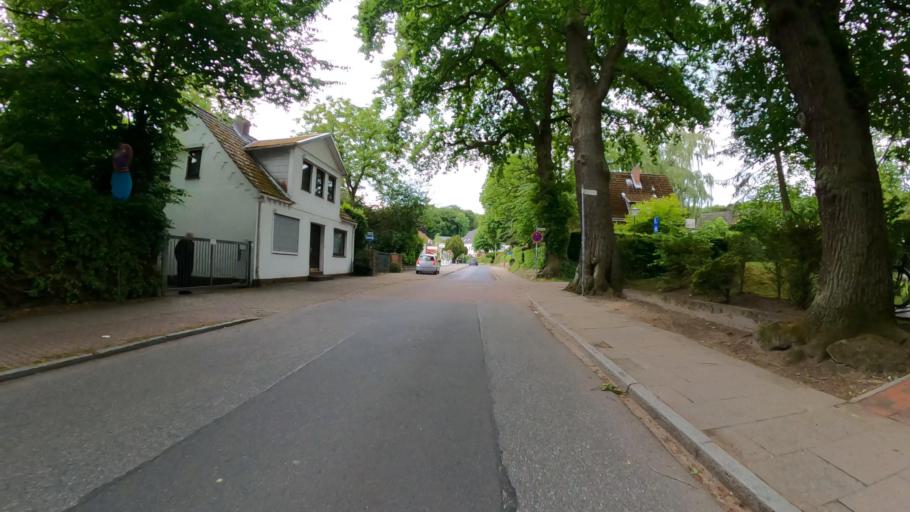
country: DE
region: Schleswig-Holstein
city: Rellingen
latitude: 53.6578
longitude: 9.8073
